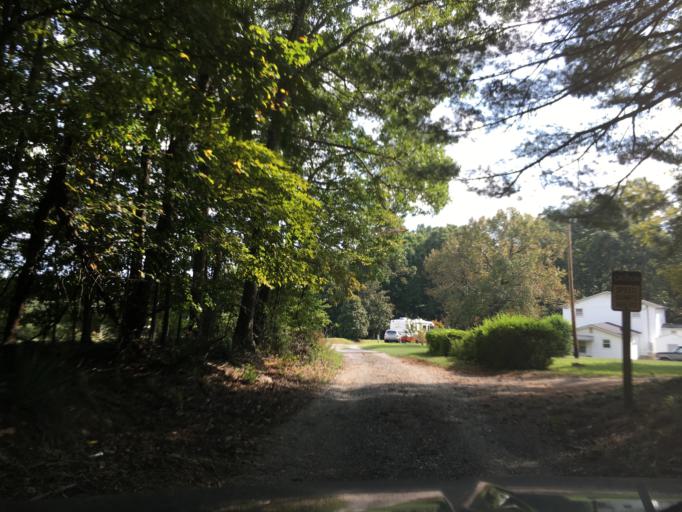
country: US
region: Virginia
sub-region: City of Lynchburg
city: West Lynchburg
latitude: 37.3325
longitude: -79.1812
